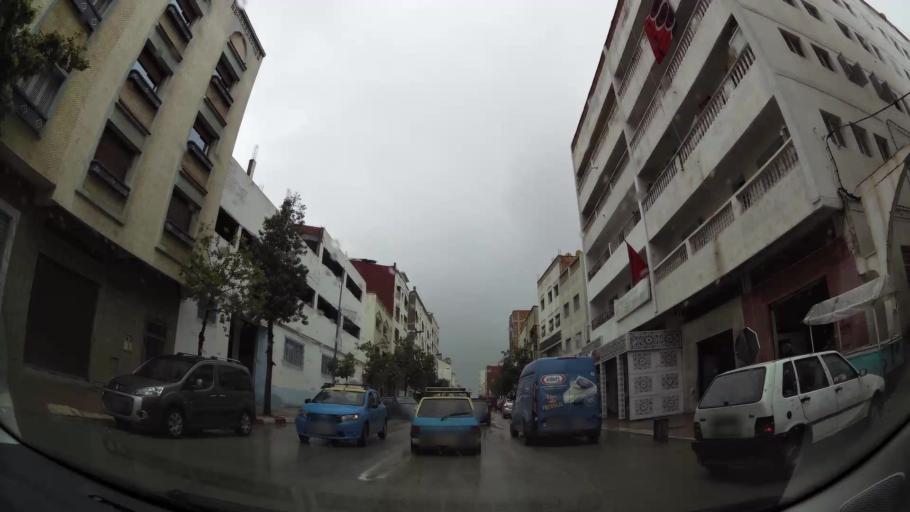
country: MA
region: Taza-Al Hoceima-Taounate
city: Al Hoceima
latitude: 35.2506
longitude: -3.9377
